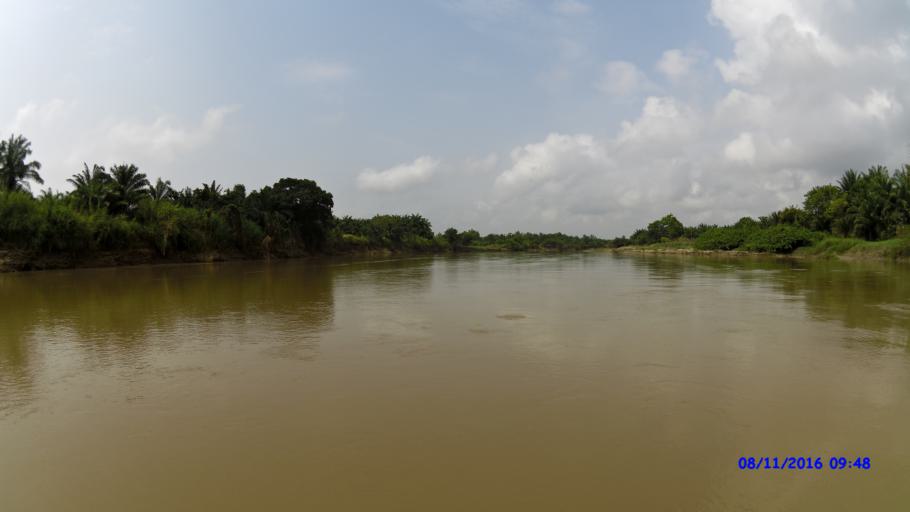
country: BJ
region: Mono
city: Come
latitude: 6.4311
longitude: 1.7718
